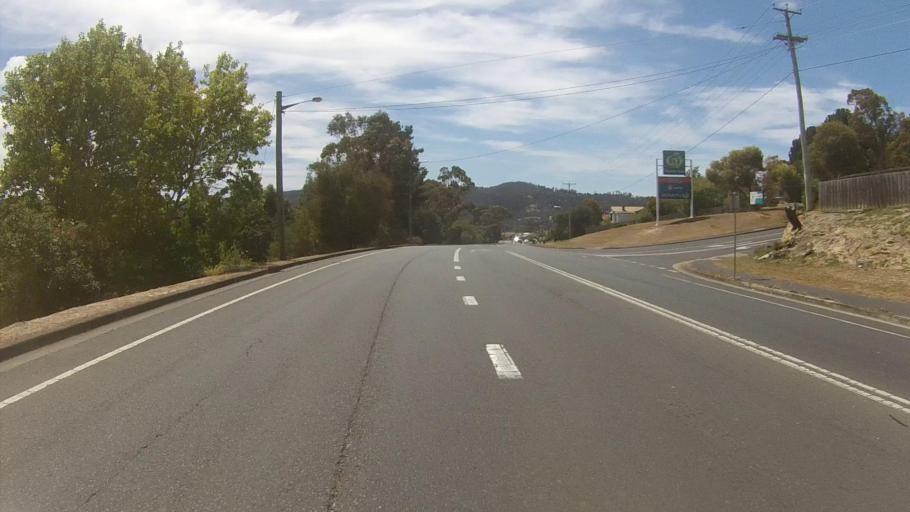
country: AU
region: Tasmania
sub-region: Kingborough
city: Kingston
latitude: -42.9792
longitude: 147.2997
